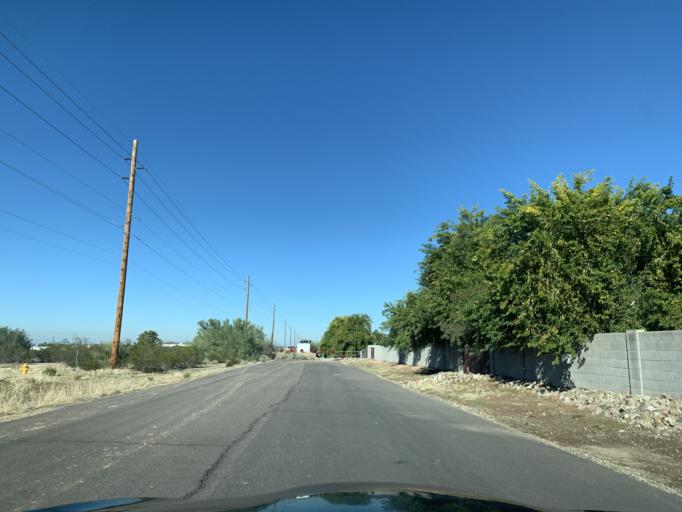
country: US
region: Arizona
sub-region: Maricopa County
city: Queen Creek
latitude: 33.2094
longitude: -111.7118
